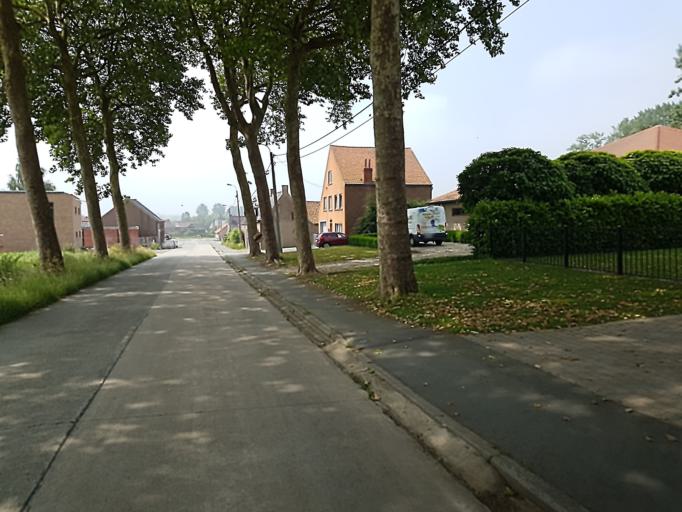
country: BE
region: Flanders
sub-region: Provincie Oost-Vlaanderen
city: Sint-Maria-Lierde
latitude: 50.8077
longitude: 3.8743
